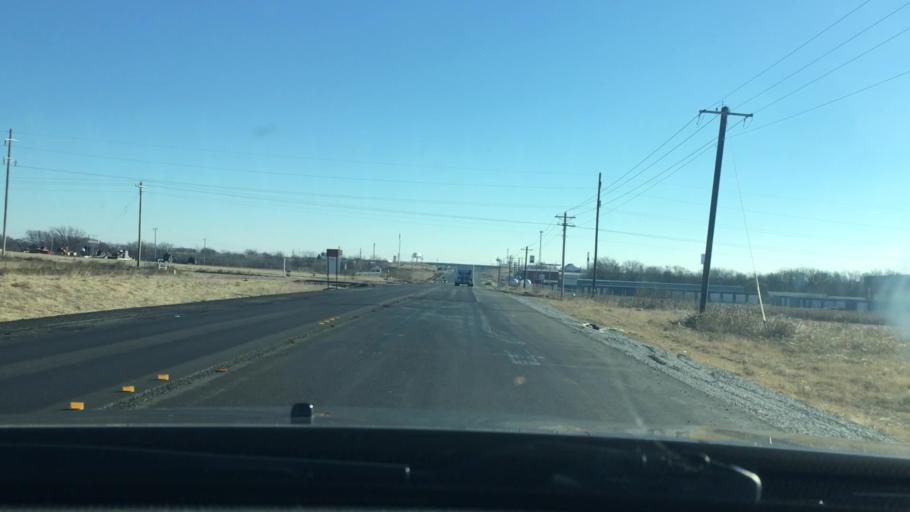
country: US
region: Oklahoma
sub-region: Love County
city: Marietta
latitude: 33.9404
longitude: -97.1445
